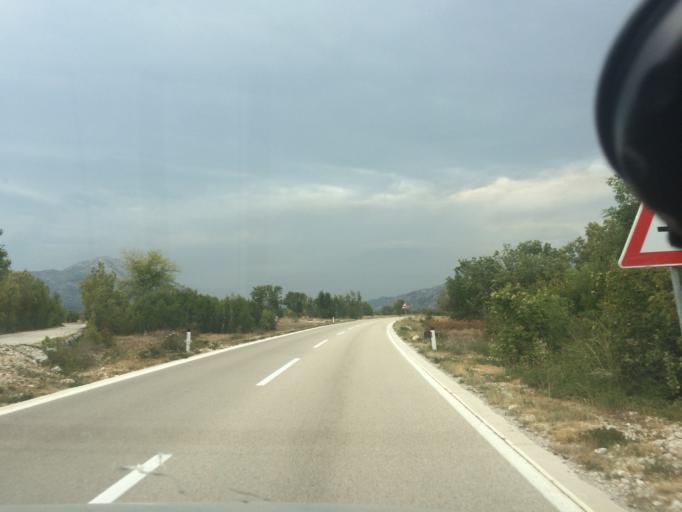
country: ME
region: Kotor
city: Risan
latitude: 42.5845
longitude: 18.6864
